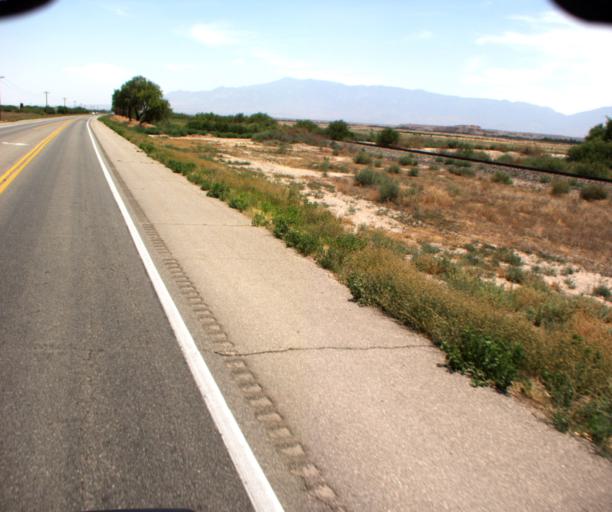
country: US
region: Arizona
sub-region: Graham County
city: Pima
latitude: 32.9903
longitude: -109.9370
